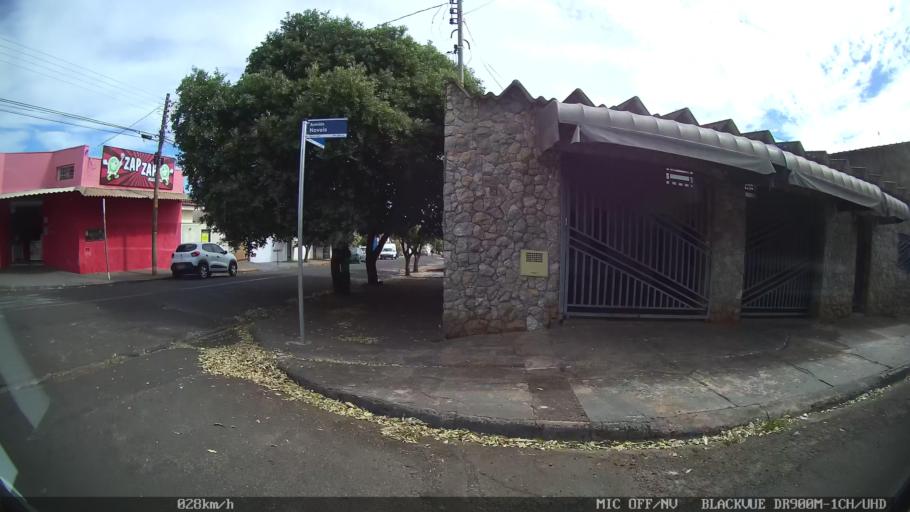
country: BR
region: Sao Paulo
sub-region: Catanduva
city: Catanduva
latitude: -21.1518
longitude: -48.9736
